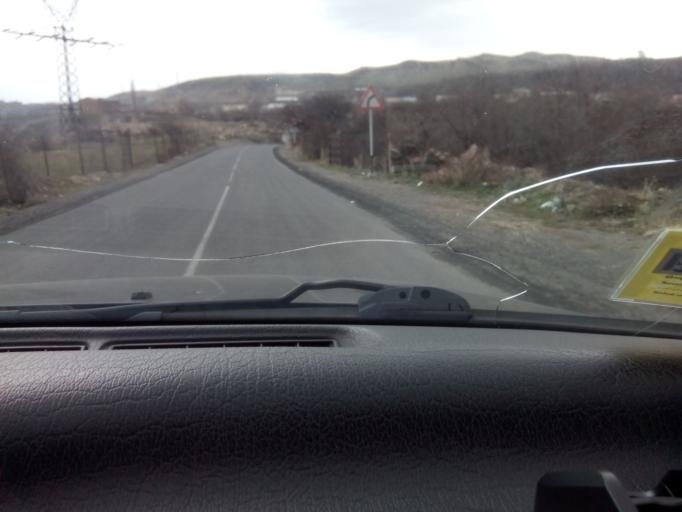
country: AM
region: Kotayk'i Marz
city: Argel
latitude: 40.3836
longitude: 44.6070
